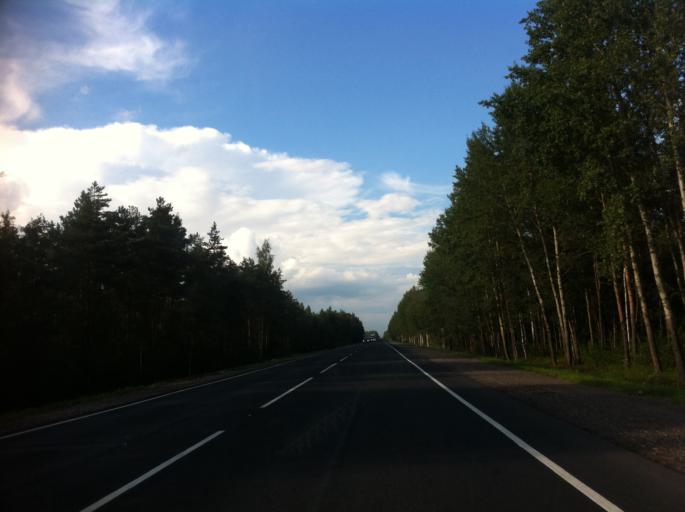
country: RU
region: Leningrad
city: Luga
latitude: 58.4428
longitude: 29.7532
